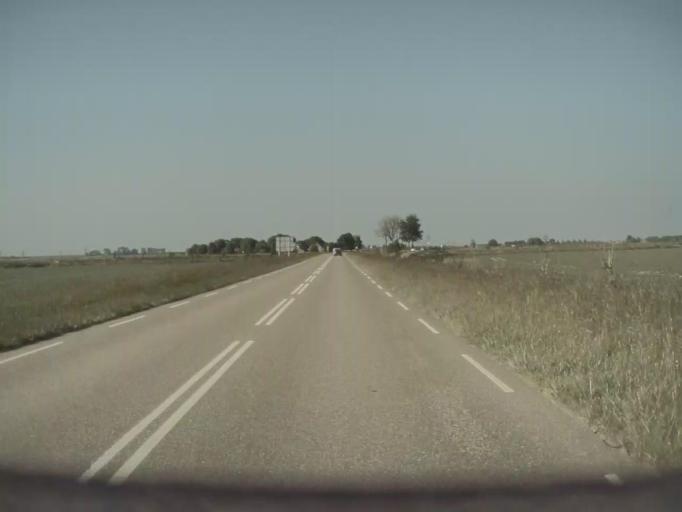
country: NL
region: Zeeland
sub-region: Gemeente Noord-Beveland
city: Kamperland
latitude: 51.5802
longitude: 3.8096
